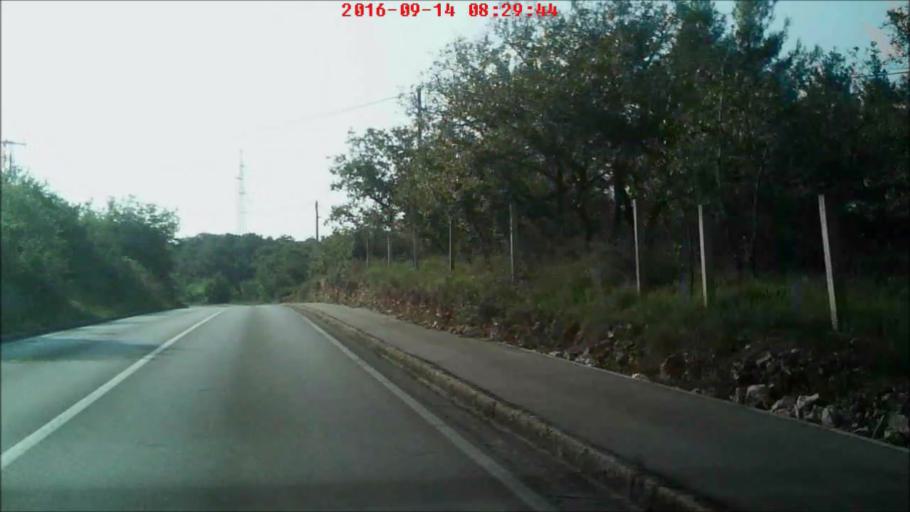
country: HR
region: Zadarska
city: Zadar
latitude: 44.1783
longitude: 15.2863
